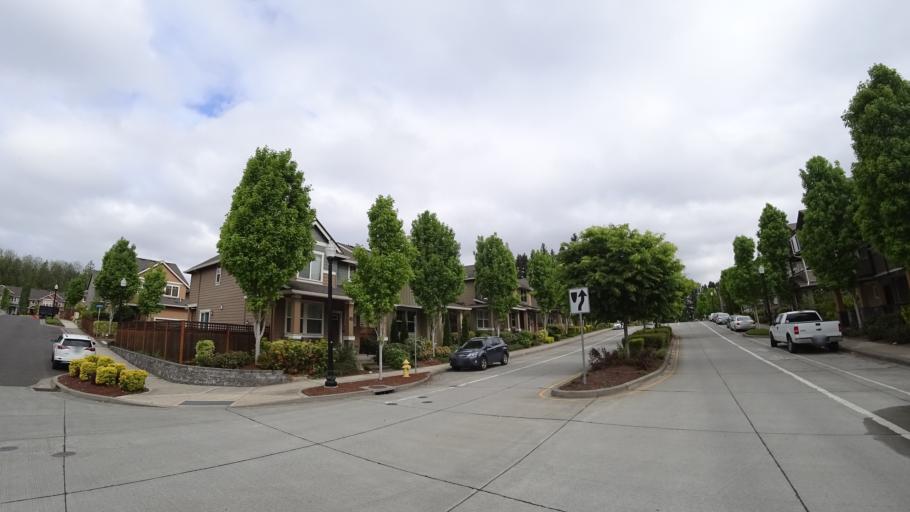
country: US
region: Oregon
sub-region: Washington County
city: Aloha
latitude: 45.5214
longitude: -122.8703
